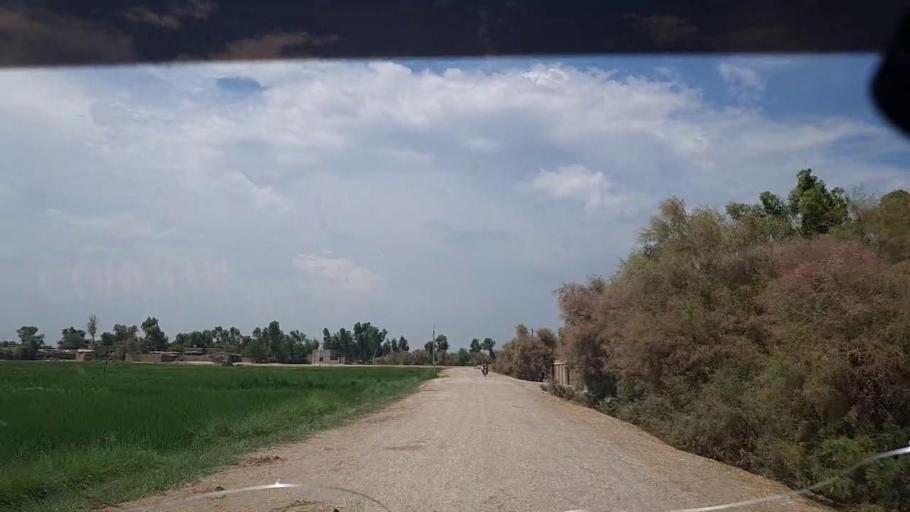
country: PK
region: Sindh
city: Ghauspur
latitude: 28.1533
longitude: 68.9973
